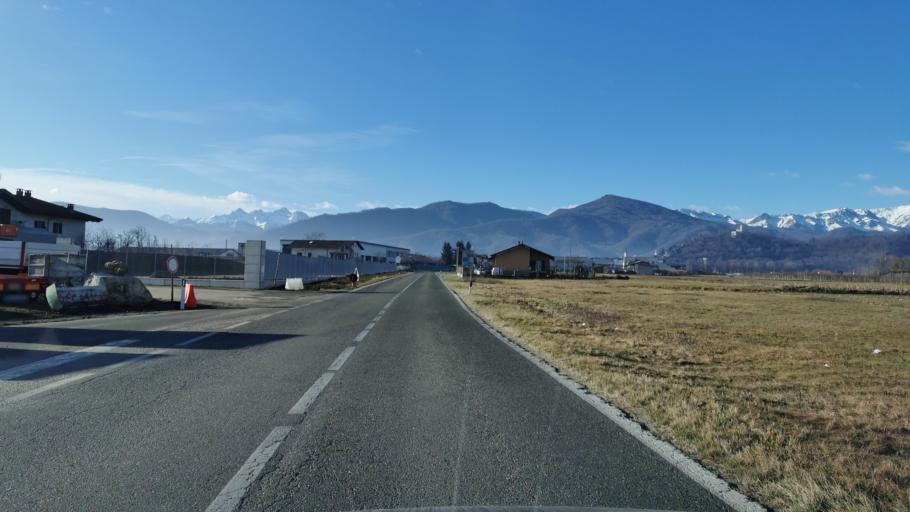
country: IT
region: Piedmont
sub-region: Provincia di Cuneo
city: Caraglio
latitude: 44.4288
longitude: 7.4463
